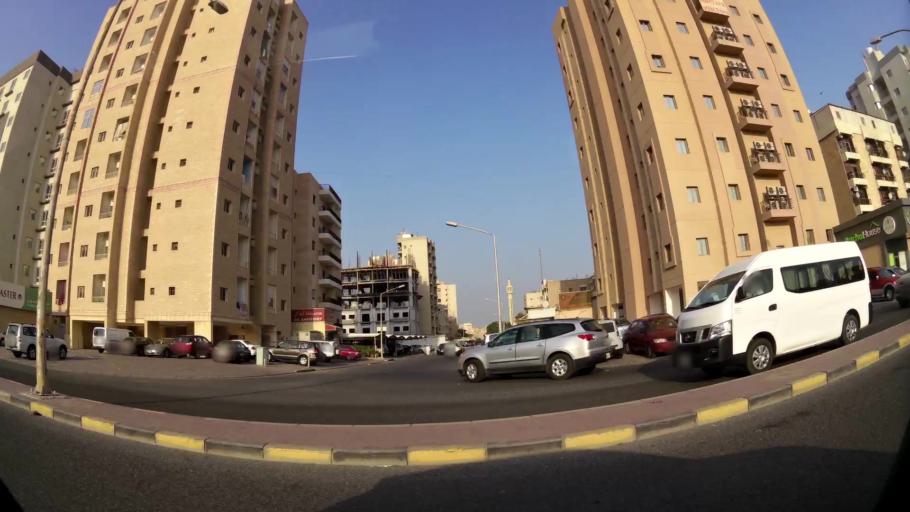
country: KW
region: Muhafazat Hawalli
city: As Salimiyah
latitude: 29.3261
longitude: 48.0682
